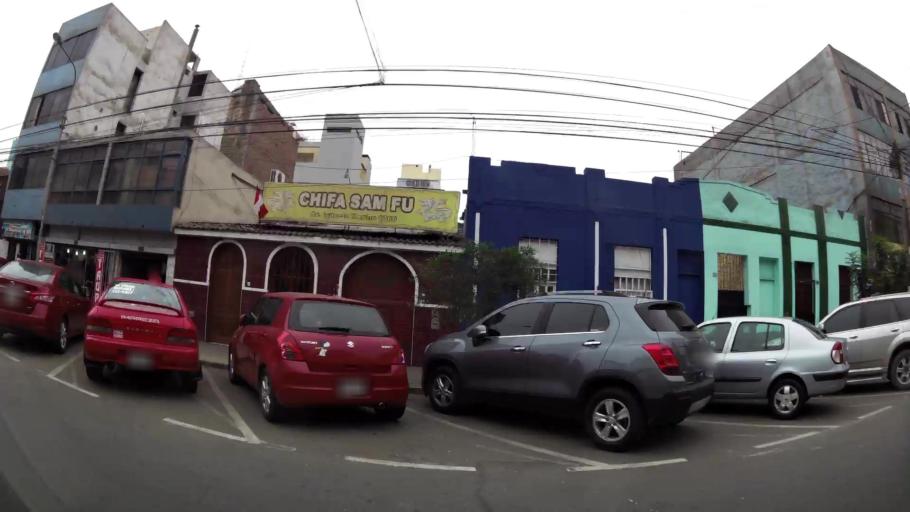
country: PE
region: Lima
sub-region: Lima
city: San Isidro
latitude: -12.0839
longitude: -77.0325
